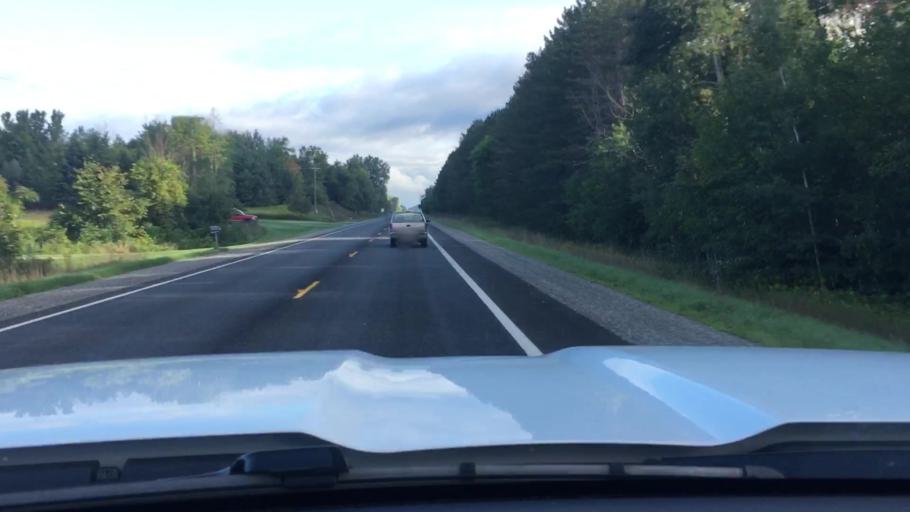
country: US
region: Michigan
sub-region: Tuscola County
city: Caro
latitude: 43.3614
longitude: -83.3829
